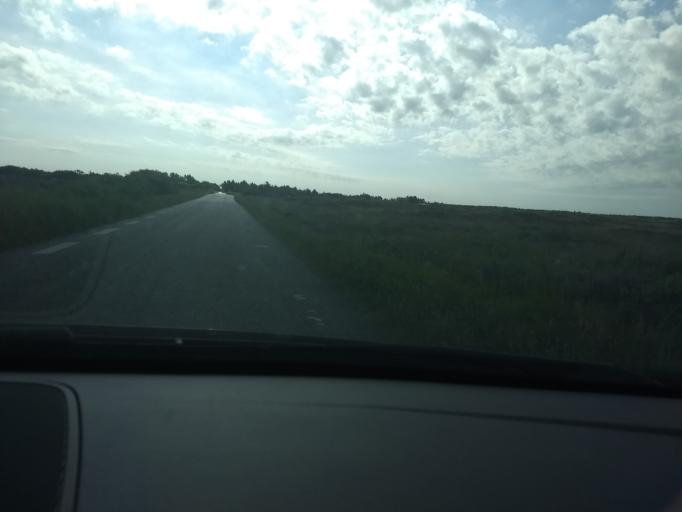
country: DE
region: Schleswig-Holstein
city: List
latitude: 55.1308
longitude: 8.5156
